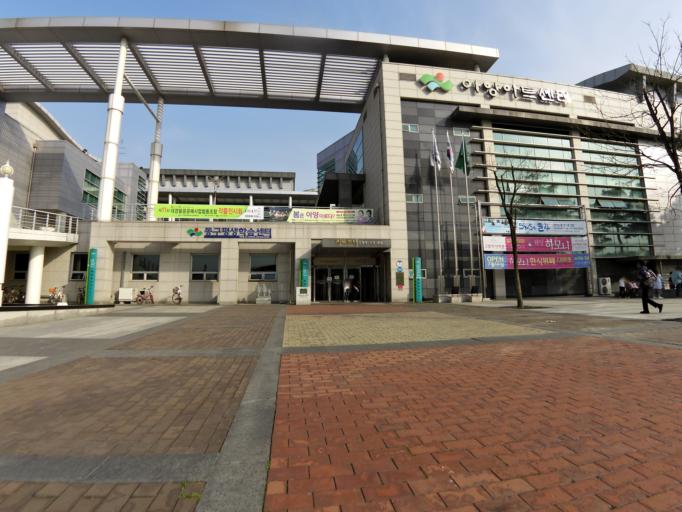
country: KR
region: Daegu
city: Daegu
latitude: 35.8799
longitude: 128.6513
